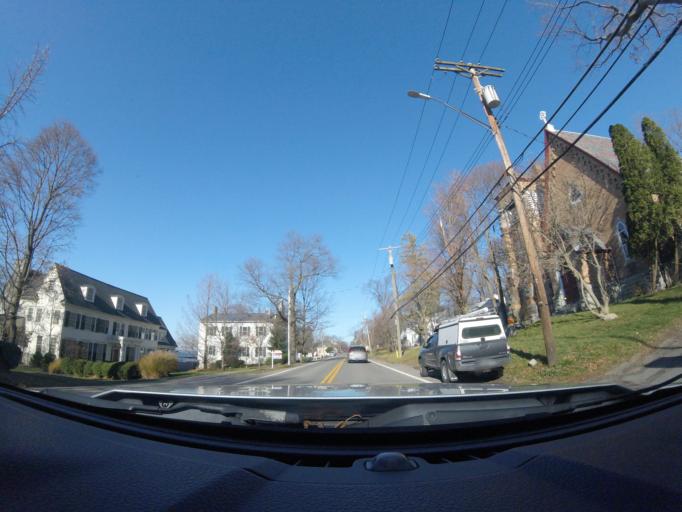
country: US
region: New York
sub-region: Cayuga County
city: Union Springs
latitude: 42.7510
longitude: -76.7015
